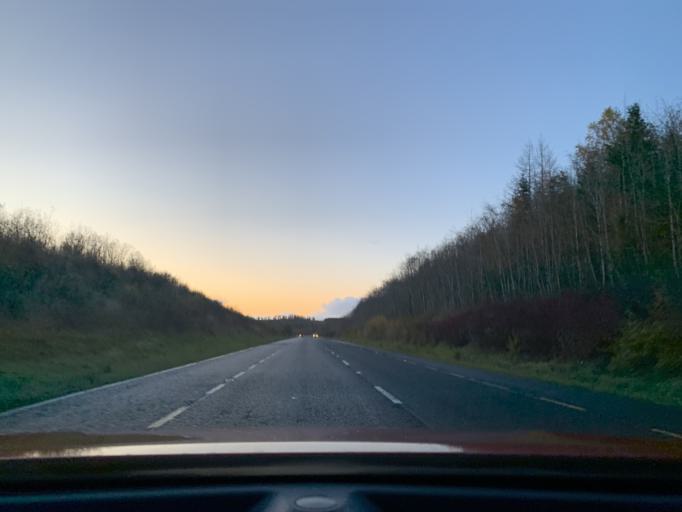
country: IE
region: Connaught
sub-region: County Leitrim
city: Carrick-on-Shannon
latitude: 53.9365
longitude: -8.0170
